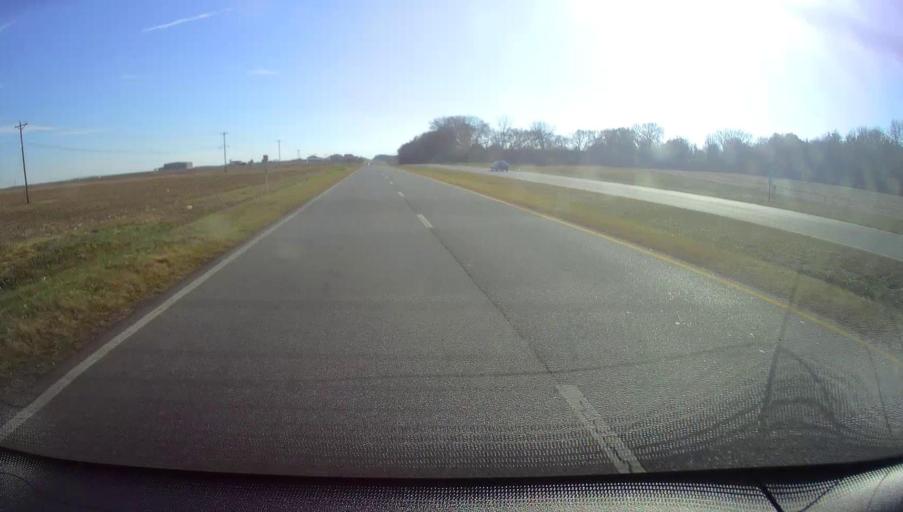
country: US
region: Alabama
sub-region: Morgan County
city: Decatur
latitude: 34.6673
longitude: -86.9500
